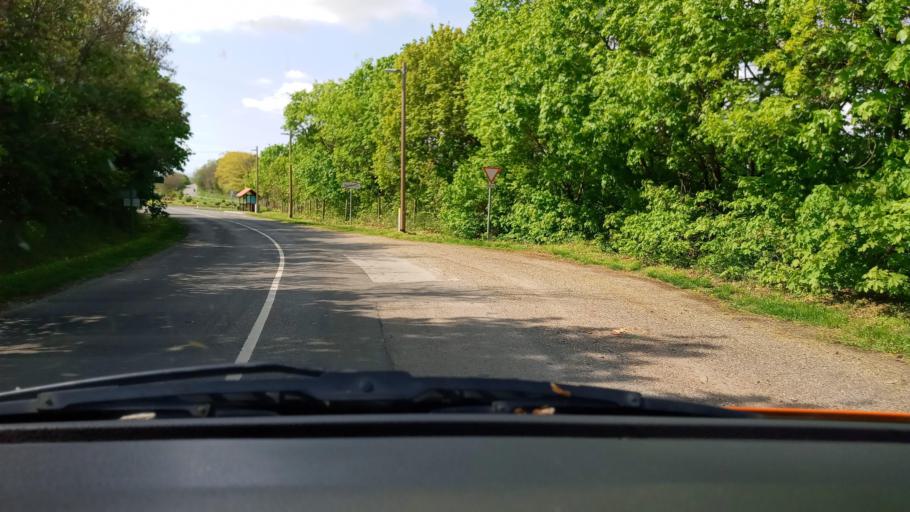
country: HU
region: Baranya
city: Hosszuheteny
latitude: 46.1460
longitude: 18.3499
